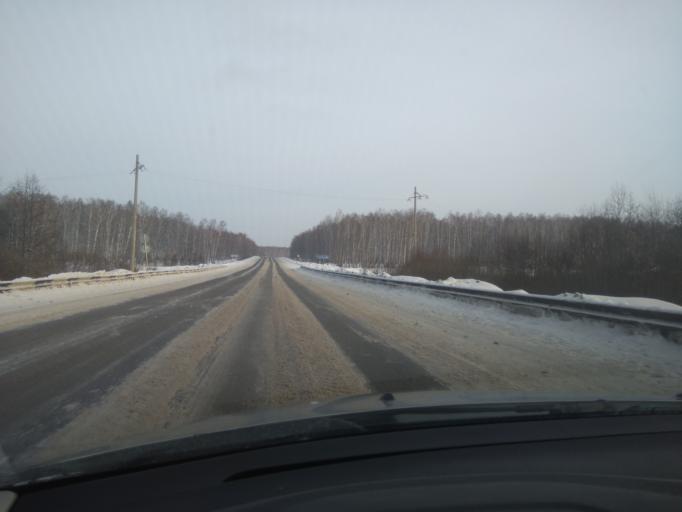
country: RU
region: Sverdlovsk
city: Bogdanovich
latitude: 56.7878
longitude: 61.9996
